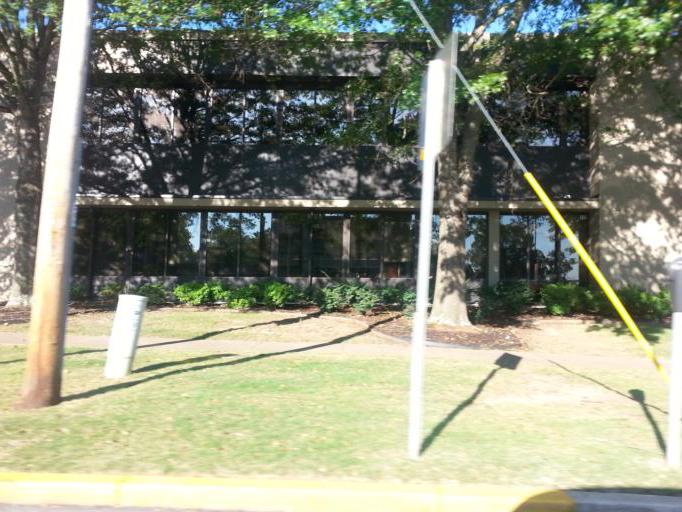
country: US
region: Alabama
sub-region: Lauderdale County
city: Florence
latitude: 34.8007
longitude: -87.6761
